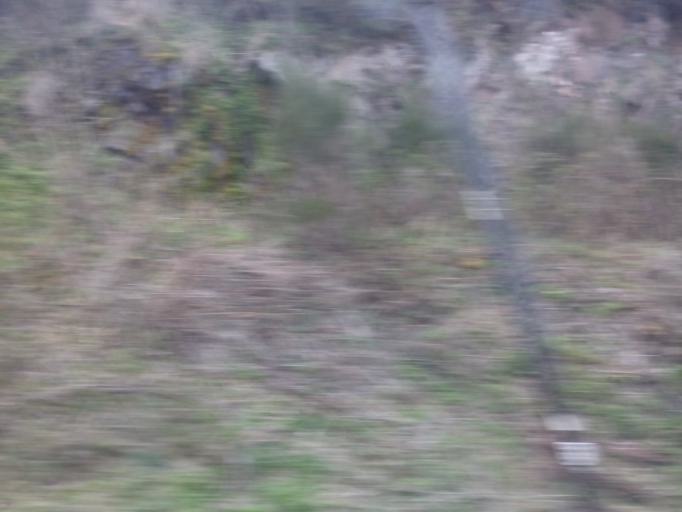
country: GB
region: Scotland
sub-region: The Scottish Borders
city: Chirnside
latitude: 55.8780
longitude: -2.2851
